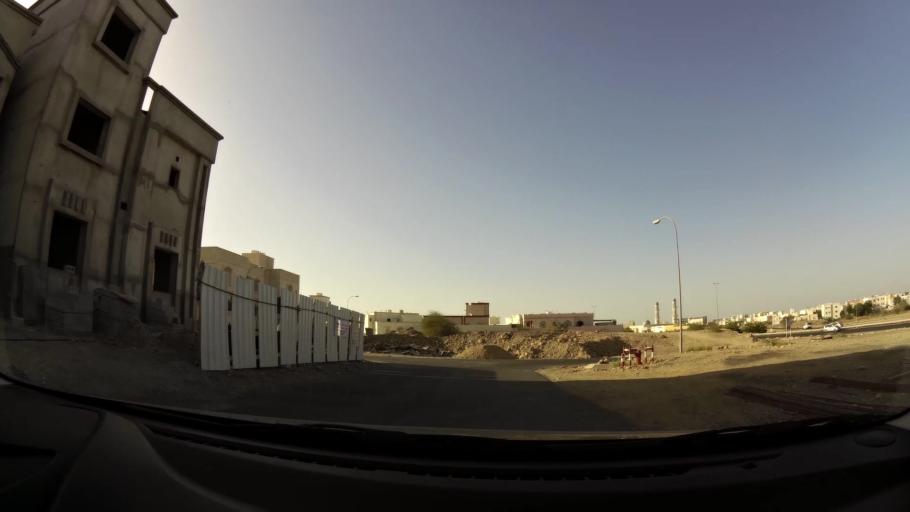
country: OM
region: Muhafazat Masqat
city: As Sib al Jadidah
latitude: 23.6045
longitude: 58.2165
